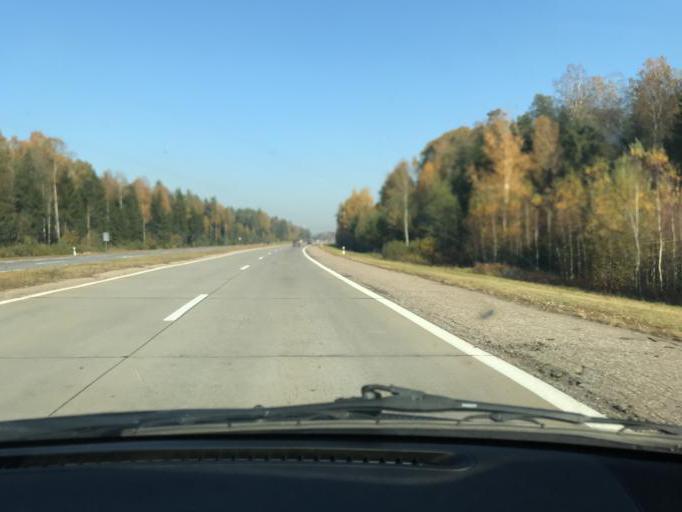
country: BY
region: Minsk
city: Uzda
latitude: 53.4108
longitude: 27.4836
